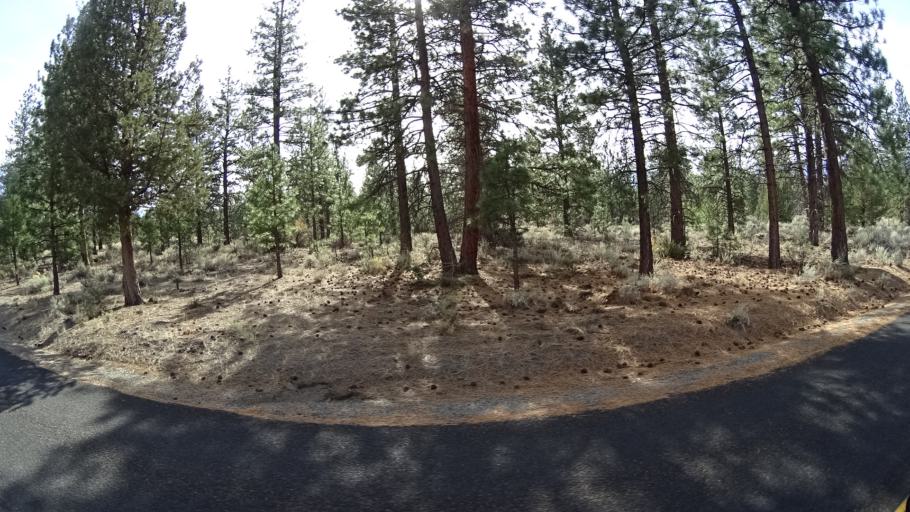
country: US
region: California
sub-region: Siskiyou County
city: Weed
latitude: 41.4981
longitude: -122.3814
